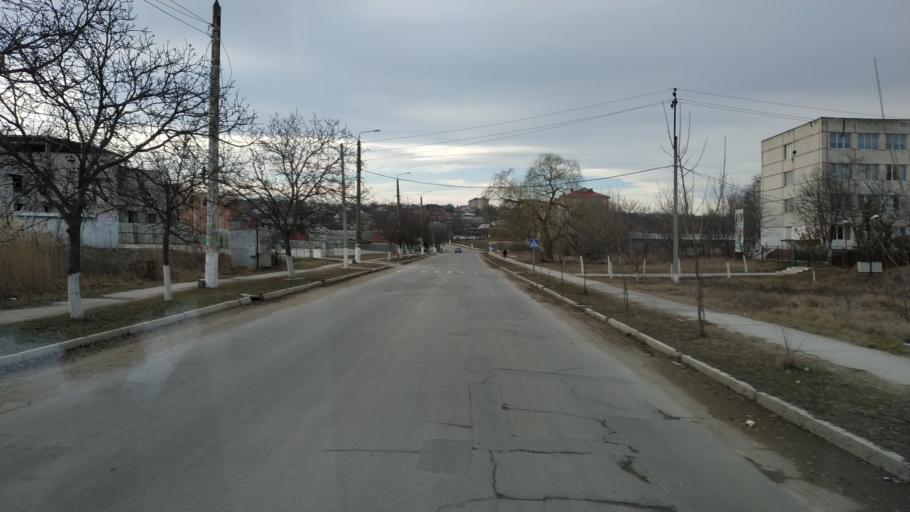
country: MD
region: Nisporeni
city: Nisporeni
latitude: 47.0822
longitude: 28.1798
